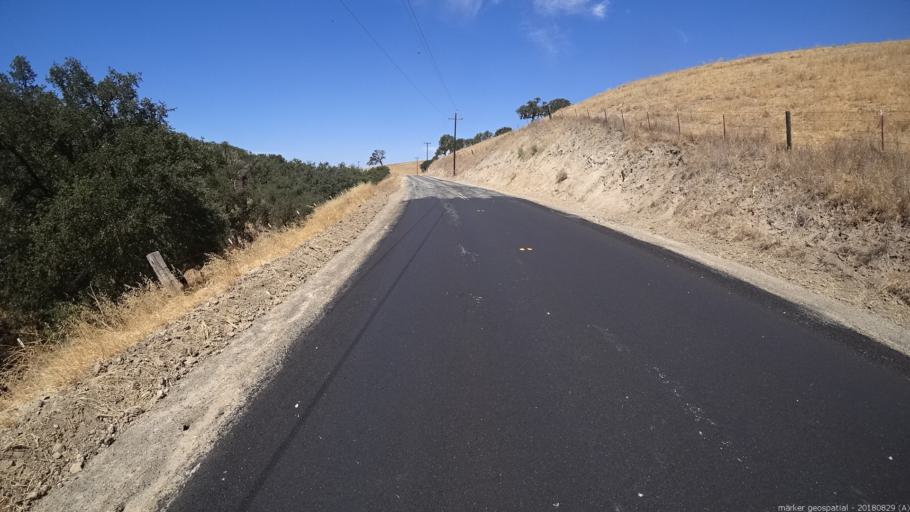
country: US
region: California
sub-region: San Luis Obispo County
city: Lake Nacimiento
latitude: 35.8241
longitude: -120.8419
